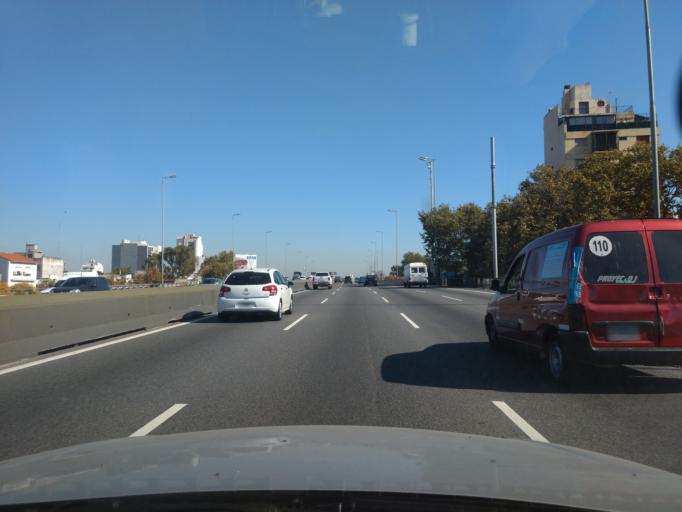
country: AR
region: Buenos Aires F.D.
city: Buenos Aires
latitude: -34.6273
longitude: -58.4153
